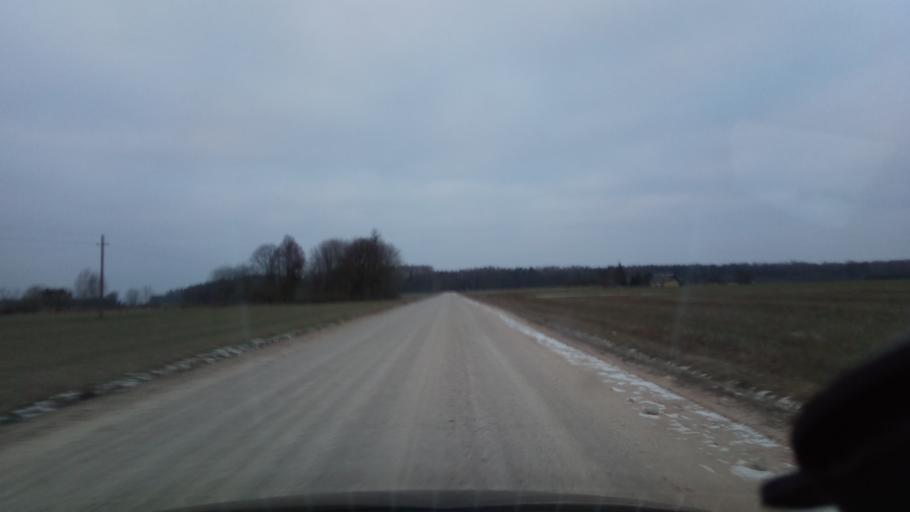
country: LT
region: Alytaus apskritis
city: Varena
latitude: 54.1178
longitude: 24.7357
